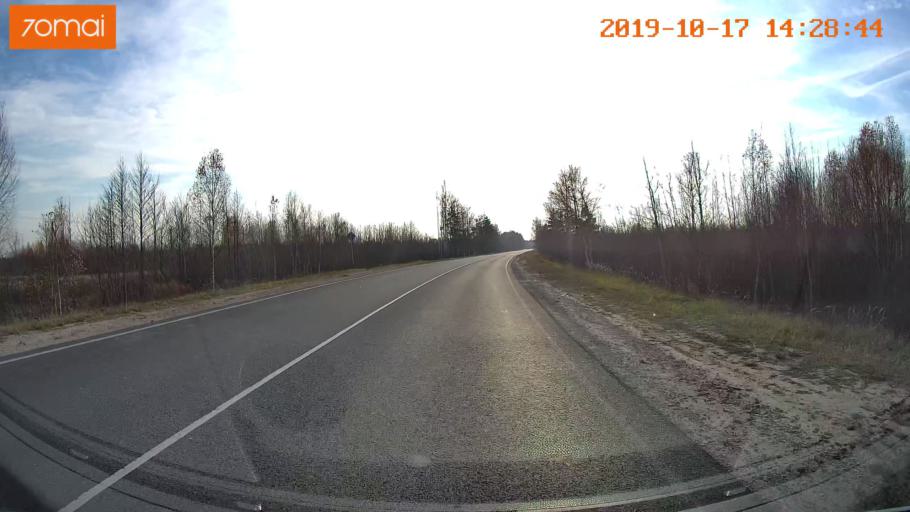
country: RU
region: Rjazan
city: Solotcha
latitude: 54.9692
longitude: 39.9509
